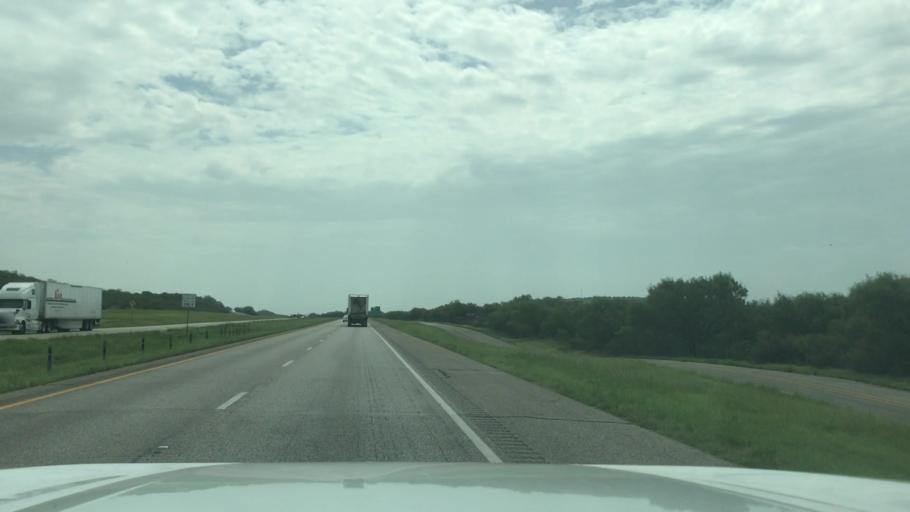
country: US
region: Texas
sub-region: Callahan County
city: Baird
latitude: 32.3714
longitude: -99.2213
